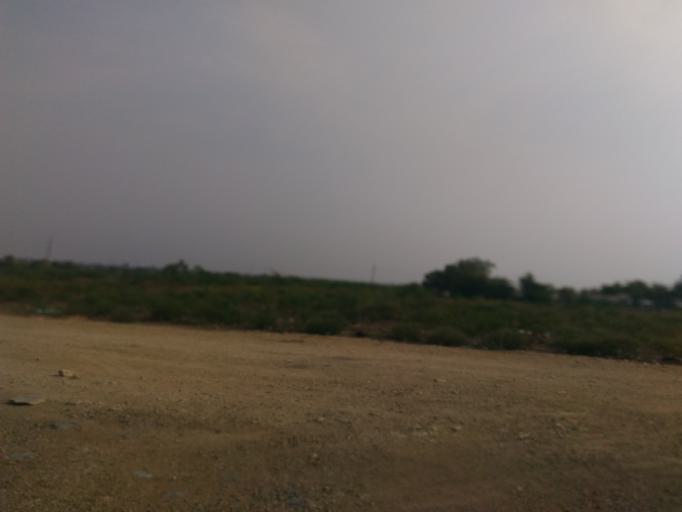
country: IN
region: Karnataka
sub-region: Raichur
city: Lingsugur
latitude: 16.1901
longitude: 76.6612
